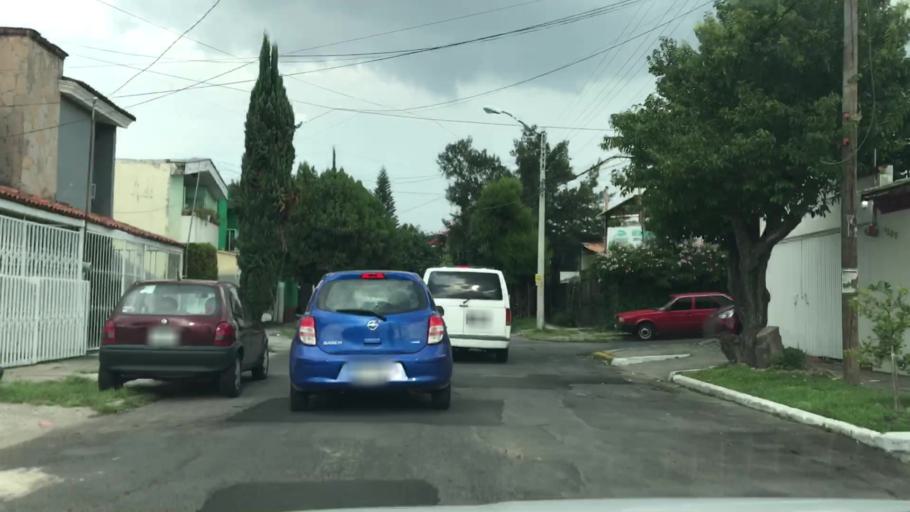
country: MX
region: Jalisco
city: Guadalajara
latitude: 20.6244
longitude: -103.4117
